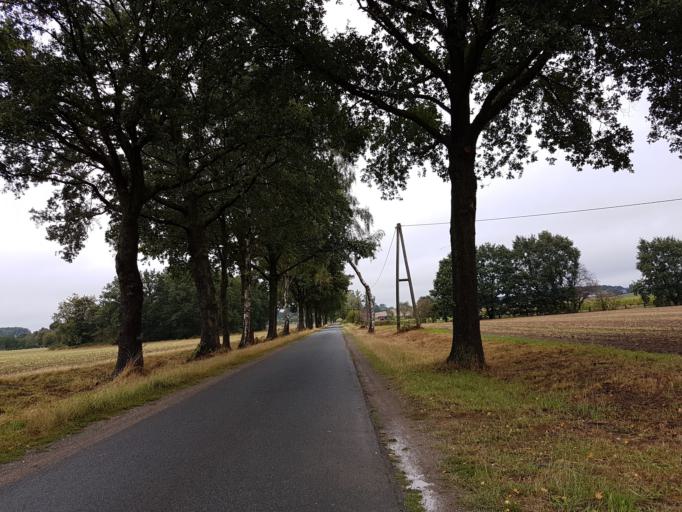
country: DE
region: North Rhine-Westphalia
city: Olfen
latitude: 51.7224
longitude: 7.3857
